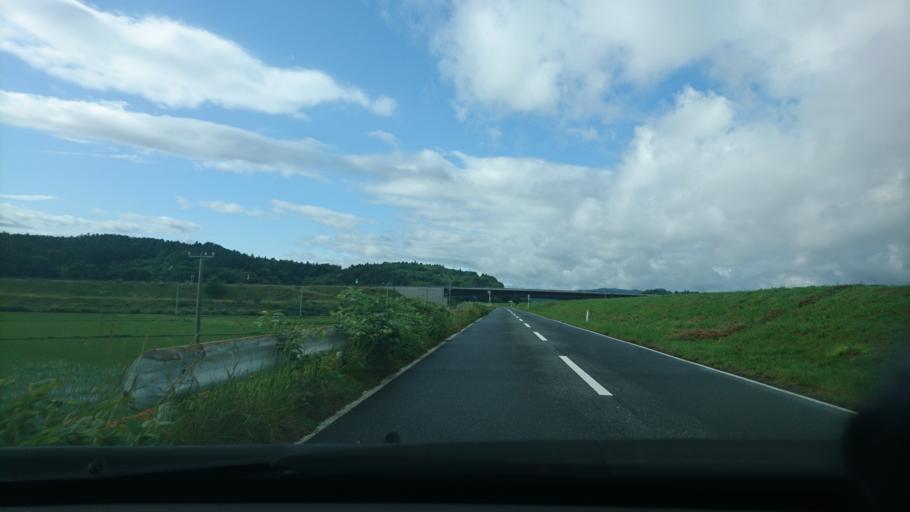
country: JP
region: Miyagi
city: Wakuya
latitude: 38.6950
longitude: 141.2851
